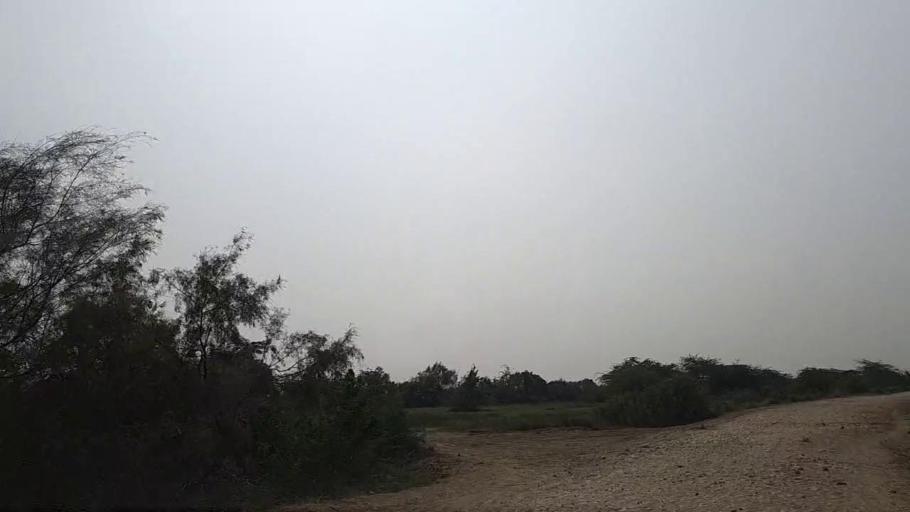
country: PK
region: Sindh
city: Mirpur Sakro
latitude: 24.6006
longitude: 67.7193
